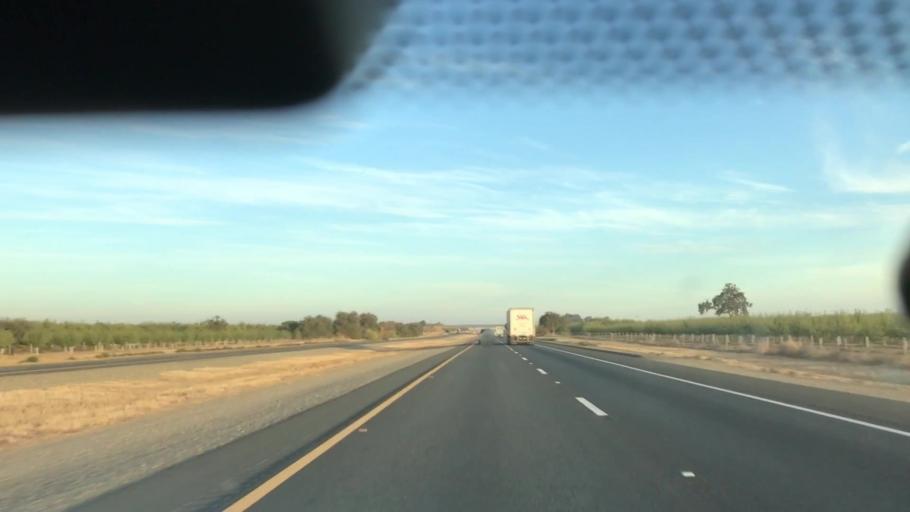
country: US
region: California
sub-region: Colusa County
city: Arbuckle
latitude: 38.9601
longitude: -122.0219
